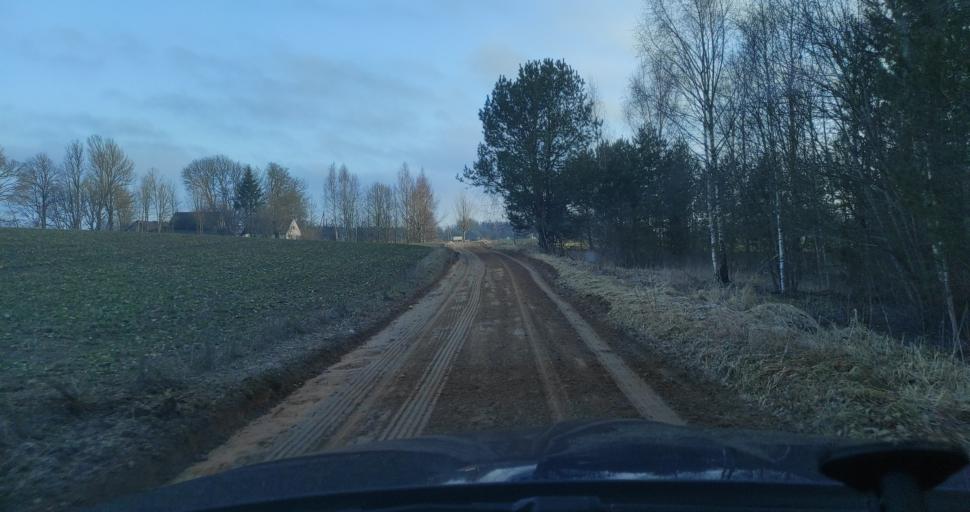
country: LV
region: Aizpute
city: Aizpute
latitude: 56.8039
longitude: 21.8044
